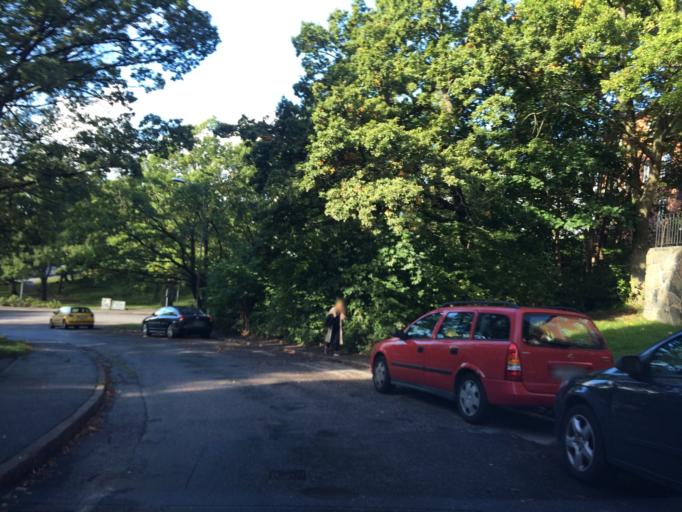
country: SE
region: Stockholm
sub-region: Stockholms Kommun
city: Arsta
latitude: 59.3042
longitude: 18.0042
